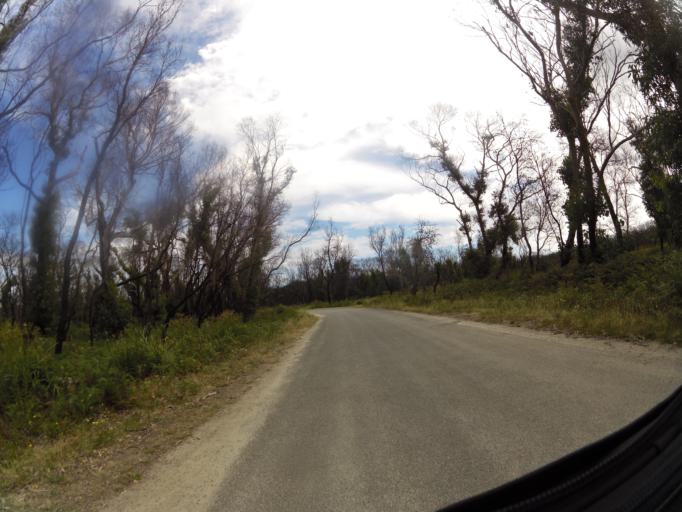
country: AU
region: Victoria
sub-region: East Gippsland
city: Lakes Entrance
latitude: -37.8009
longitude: 148.7406
